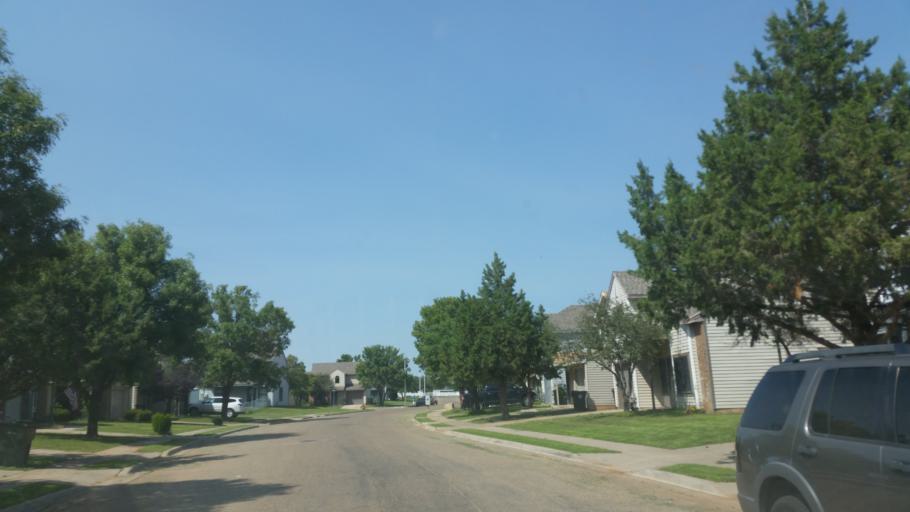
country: US
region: New Mexico
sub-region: Curry County
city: Clovis
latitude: 34.4461
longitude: -103.1734
